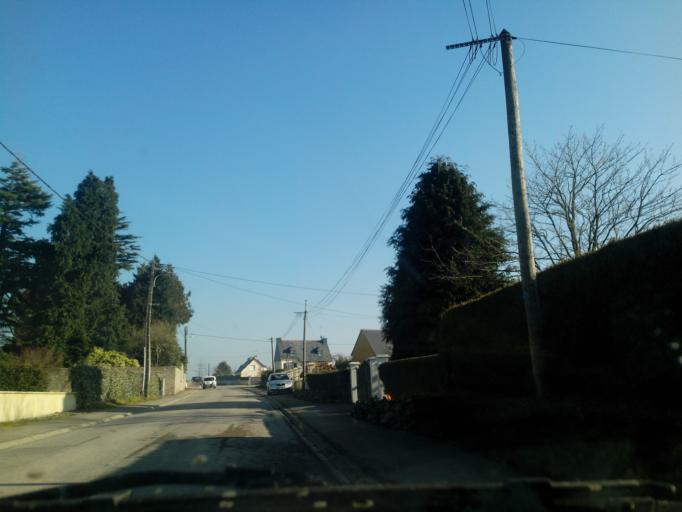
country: FR
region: Brittany
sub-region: Departement du Morbihan
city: Meneac
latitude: 48.1388
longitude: -2.4544
